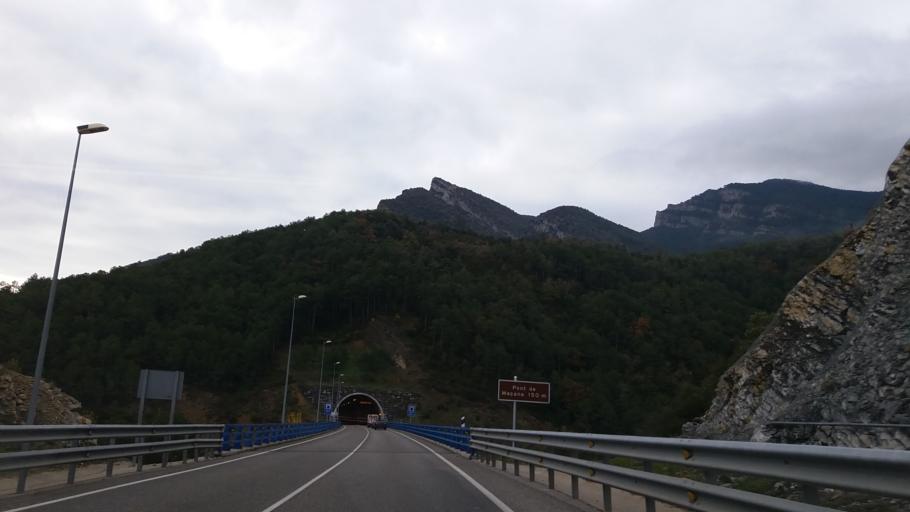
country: ES
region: Catalonia
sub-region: Provincia de Lleida
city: Coll de Nargo
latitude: 42.1498
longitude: 1.3071
